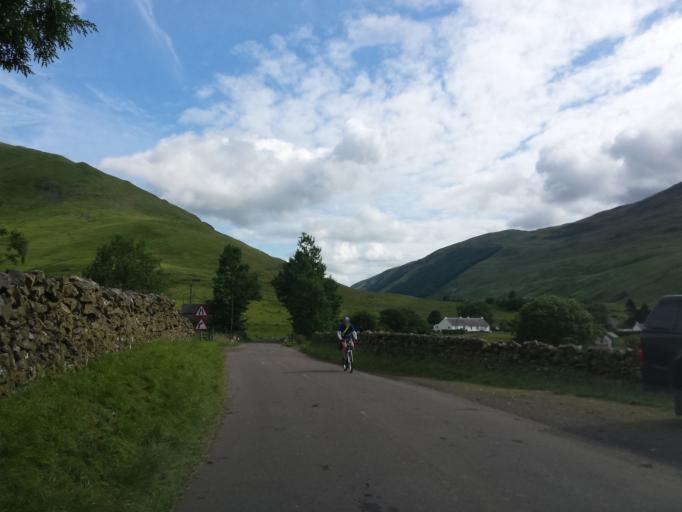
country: GB
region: Scotland
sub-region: Dumfries and Galloway
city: Moffat
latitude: 55.3739
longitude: -3.3510
